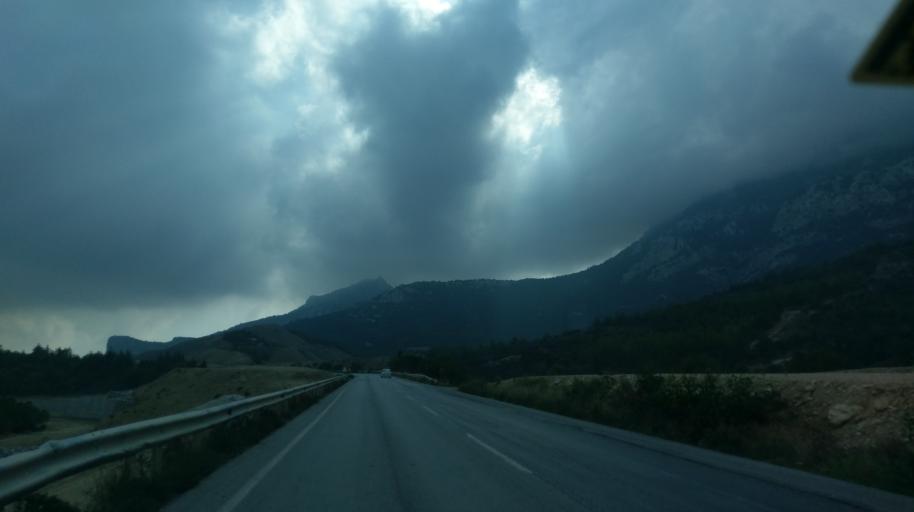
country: CY
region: Keryneia
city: Kyrenia
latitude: 35.3007
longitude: 33.4312
